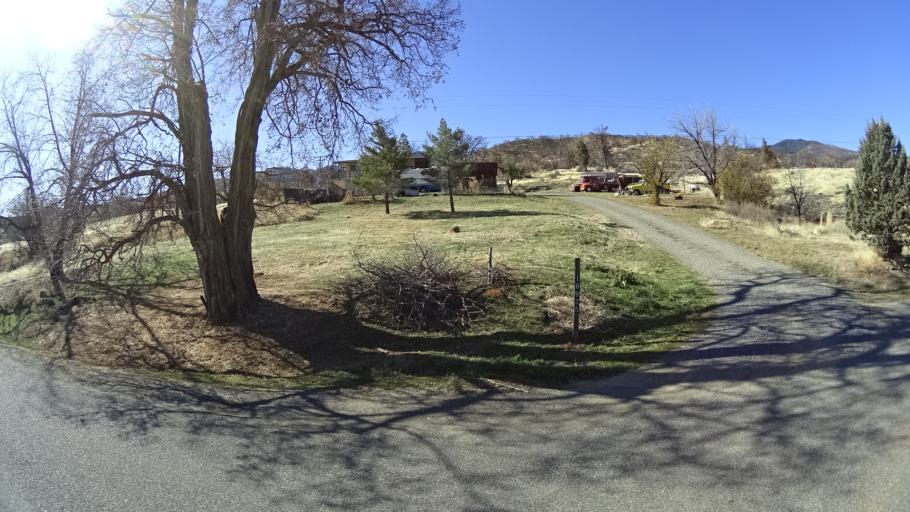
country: US
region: California
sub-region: Siskiyou County
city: Yreka
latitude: 41.9289
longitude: -122.5842
